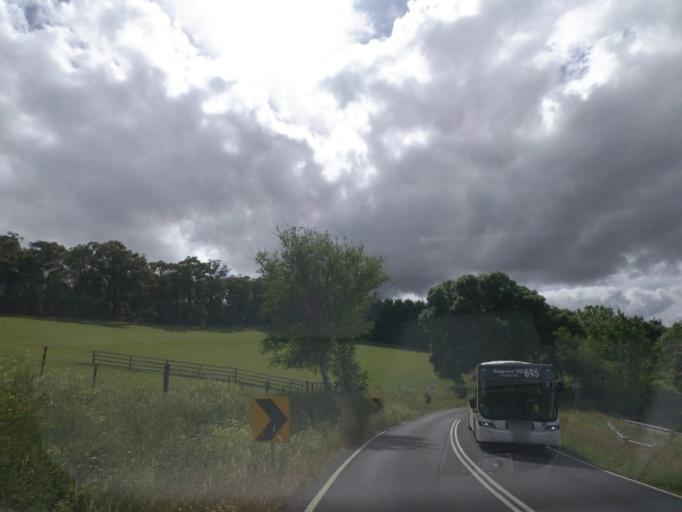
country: AU
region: Victoria
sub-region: Cardinia
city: Cockatoo
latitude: -37.9238
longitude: 145.4789
